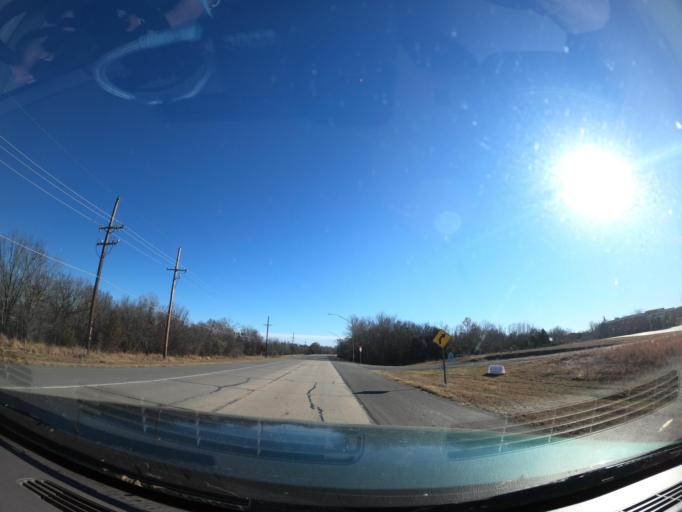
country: US
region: Oklahoma
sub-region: McIntosh County
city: Eufaula
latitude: 35.2999
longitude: -95.5841
